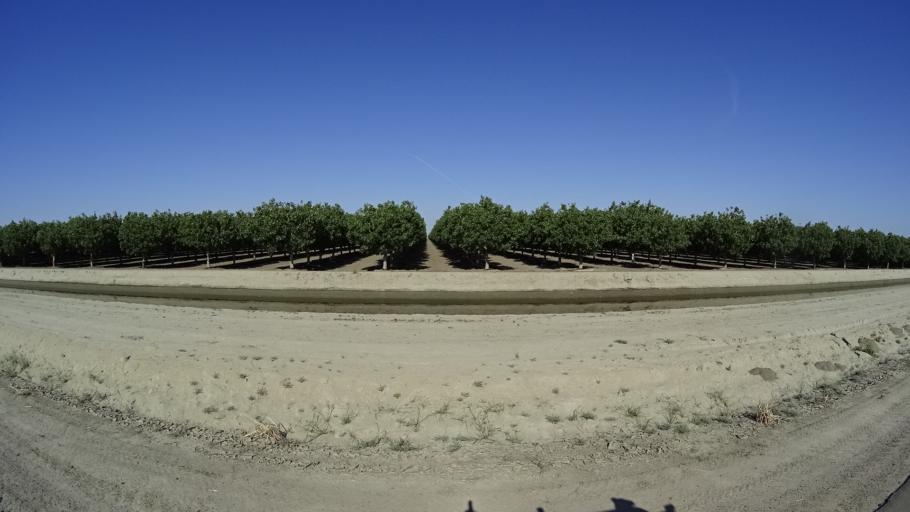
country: US
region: California
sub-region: Kings County
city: Corcoran
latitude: 36.0850
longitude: -119.5899
